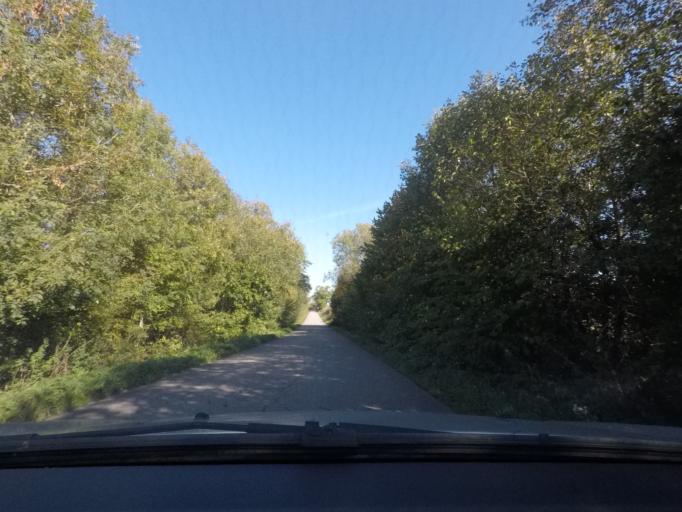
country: BE
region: Wallonia
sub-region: Province du Luxembourg
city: Etalle
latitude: 49.7136
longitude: 5.5662
